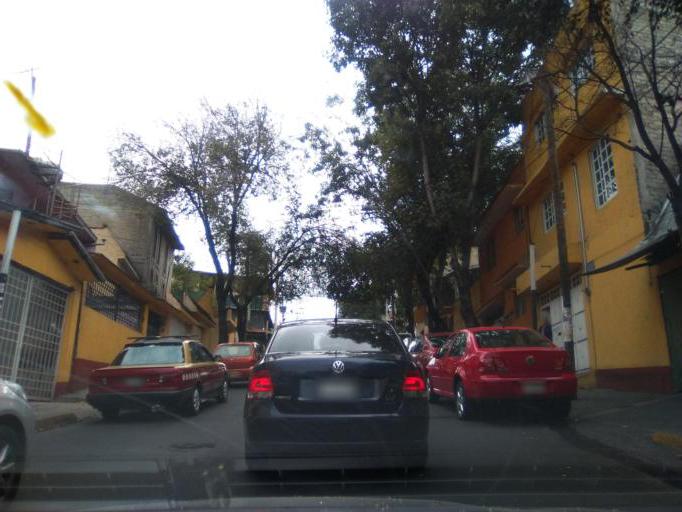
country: MX
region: Mexico City
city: Alvaro Obregon
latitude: 19.3730
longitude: -99.2128
